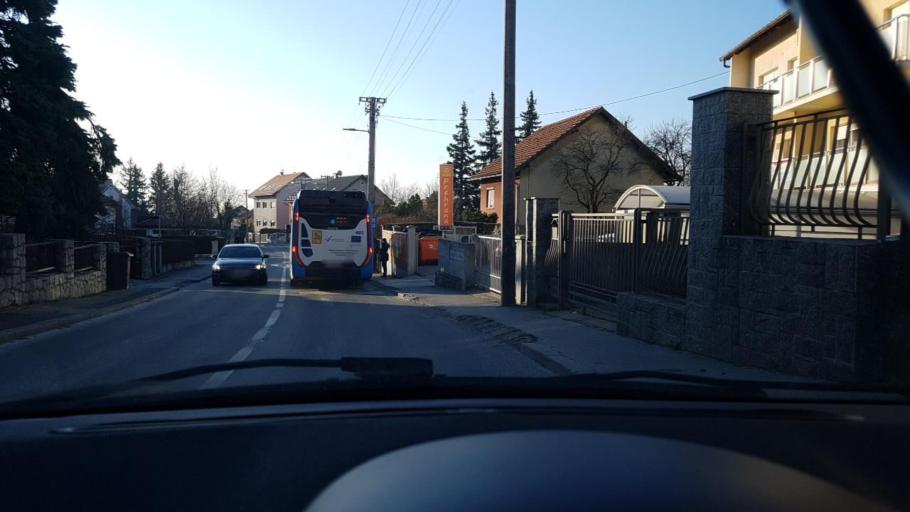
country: HR
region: Grad Zagreb
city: Zagreb
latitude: 45.8403
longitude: 16.0016
